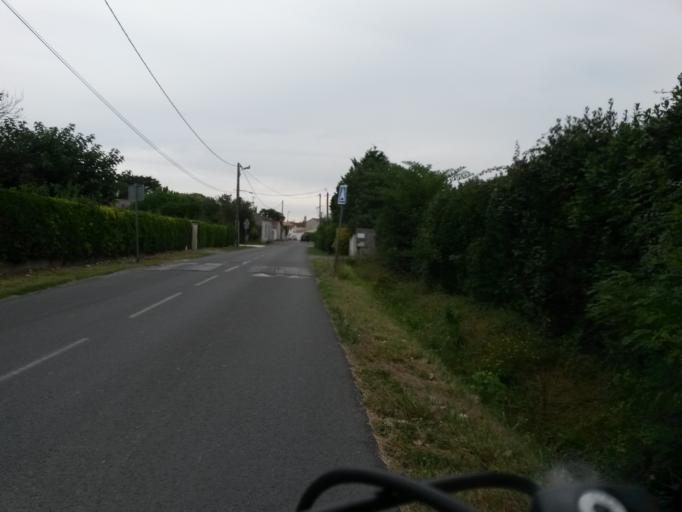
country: FR
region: Poitou-Charentes
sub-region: Departement de la Charente-Maritime
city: Dolus-d'Oleron
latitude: 45.9428
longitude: -1.3188
